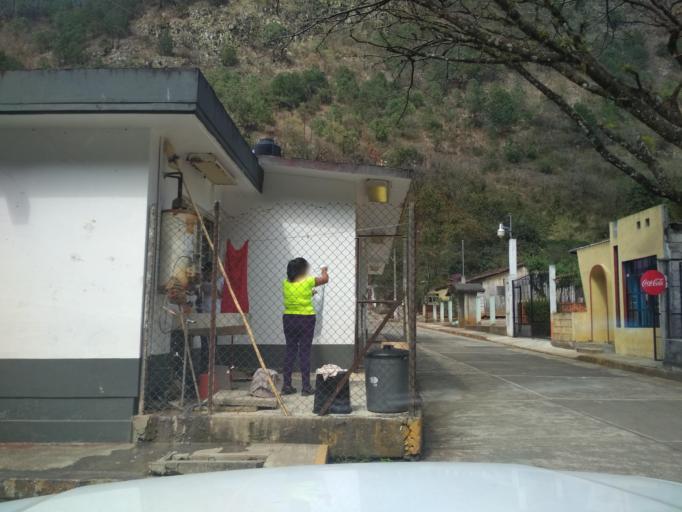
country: MX
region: Veracruz
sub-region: Tlilapan
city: Tonalixco
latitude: 18.7885
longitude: -97.0933
